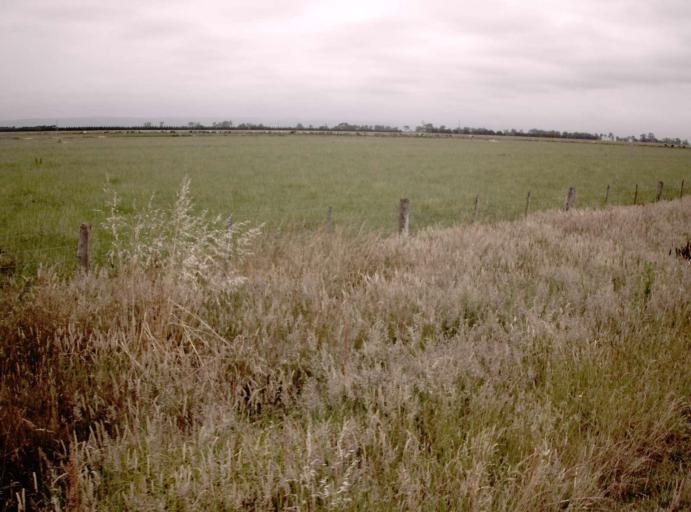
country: AU
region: Victoria
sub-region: Wellington
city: Heyfield
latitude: -38.0754
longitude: 146.7708
